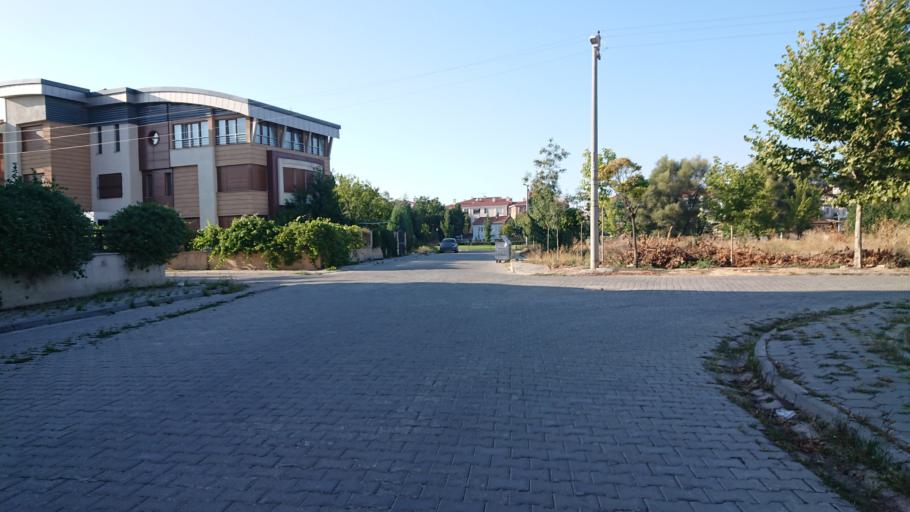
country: TR
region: Eskisehir
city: Eskisehir
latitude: 39.7668
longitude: 30.4927
